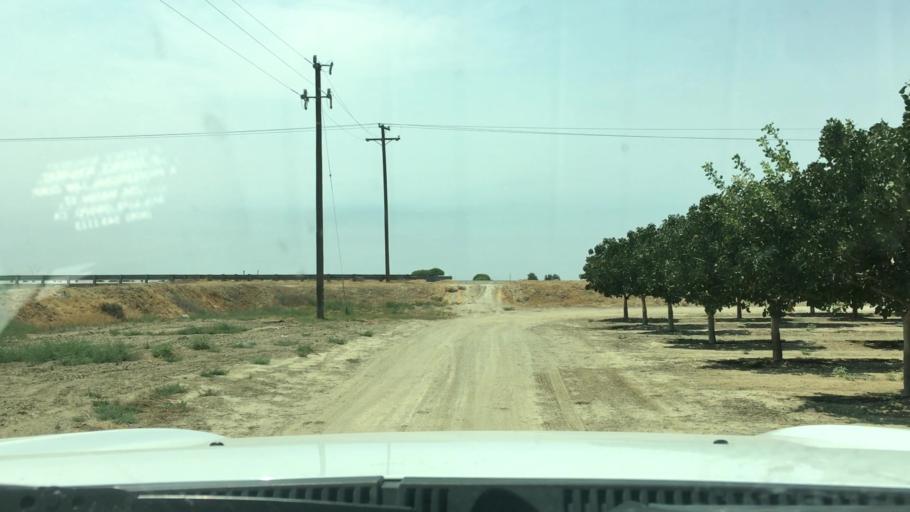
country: US
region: California
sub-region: Kern County
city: Wasco
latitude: 35.6813
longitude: -119.4366
